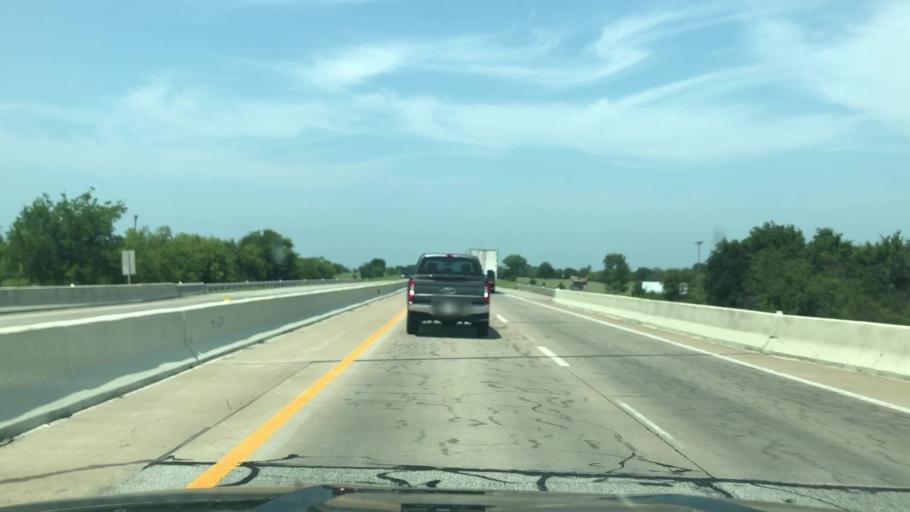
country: US
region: Oklahoma
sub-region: Ottawa County
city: Fairland
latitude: 36.7850
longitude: -94.8877
